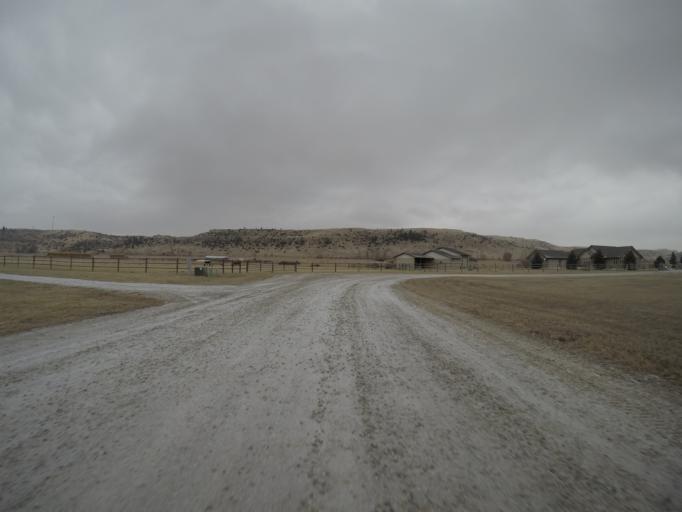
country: US
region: Montana
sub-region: Stillwater County
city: Absarokee
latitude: 45.5277
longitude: -109.4653
